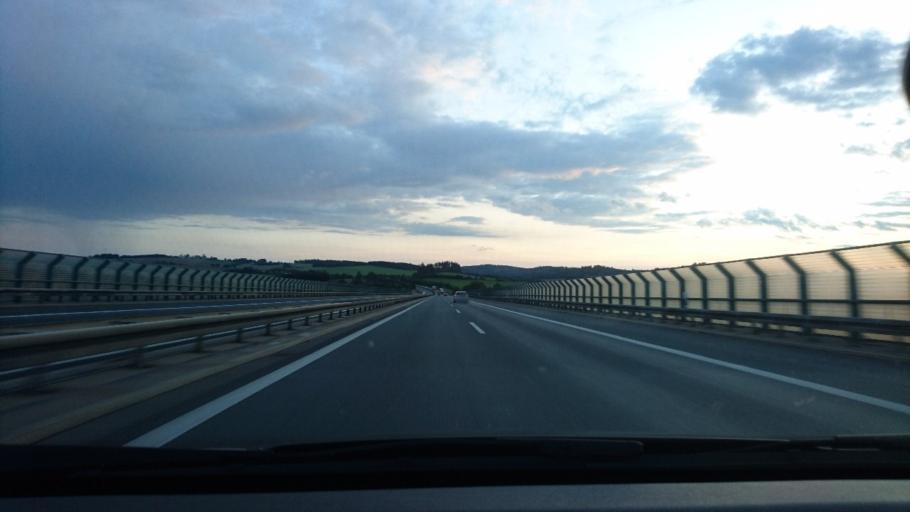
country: DE
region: Saxony
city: Weischlitz
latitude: 50.4287
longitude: 12.0714
